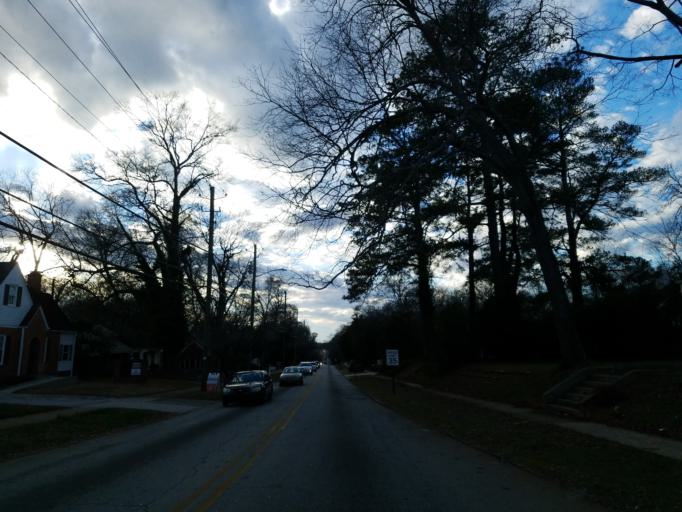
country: US
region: Georgia
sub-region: Henry County
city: McDonough
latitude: 33.4478
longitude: -84.1483
